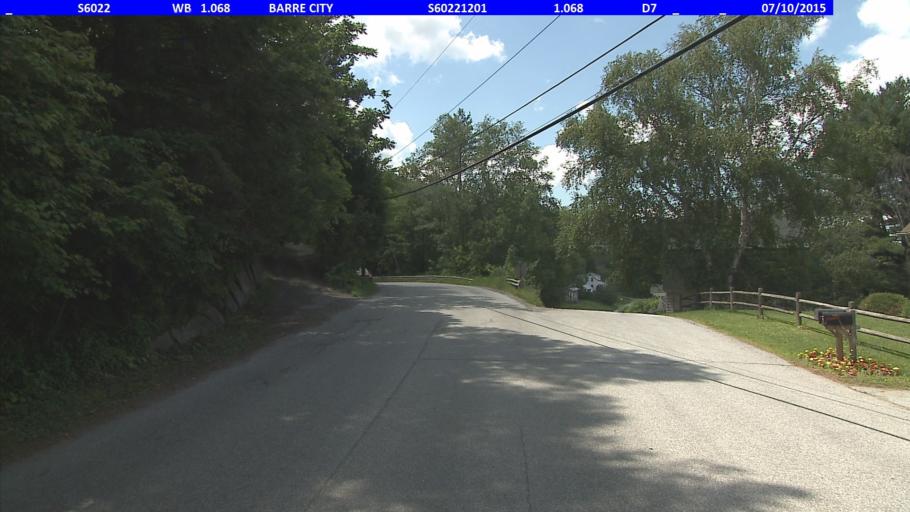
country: US
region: Vermont
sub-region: Washington County
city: Barre
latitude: 44.1944
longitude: -72.5071
